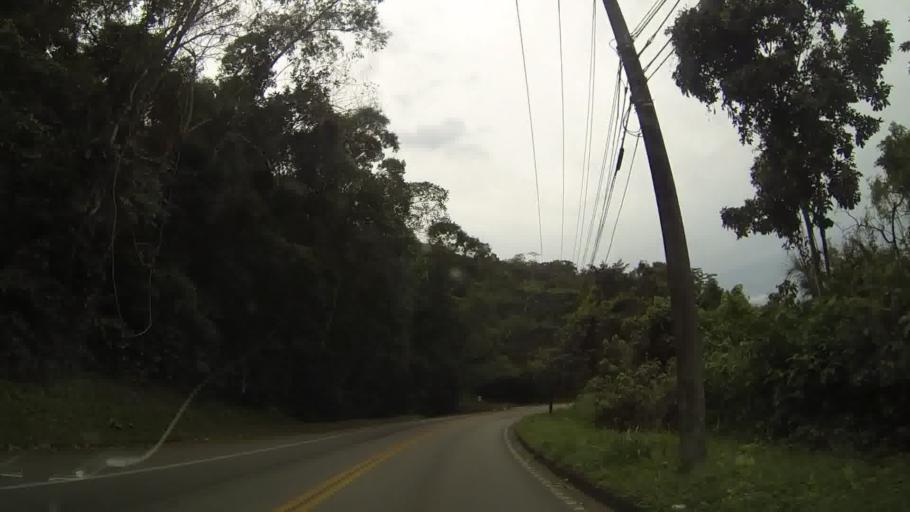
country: BR
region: Sao Paulo
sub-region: Sao Sebastiao
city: Sao Sebastiao
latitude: -23.8141
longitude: -45.4644
